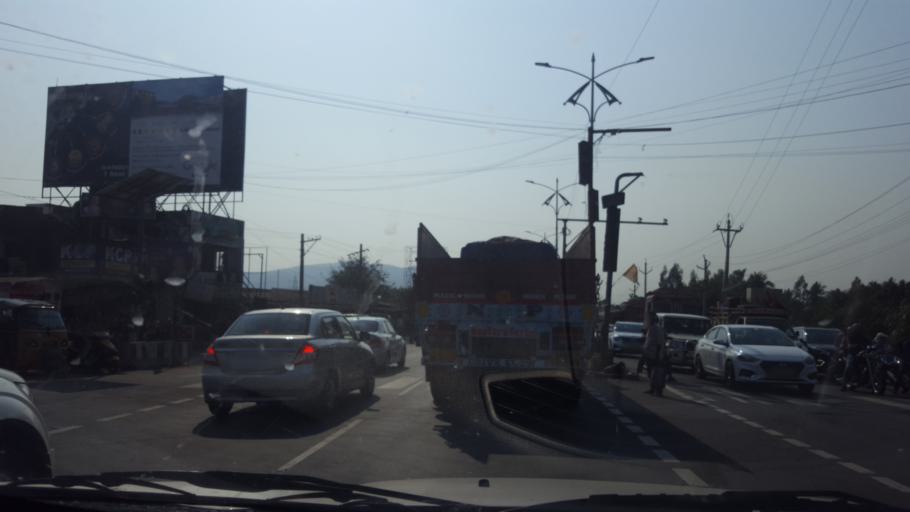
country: IN
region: Andhra Pradesh
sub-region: Vishakhapatnam
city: Anakapalle
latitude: 17.6879
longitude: 83.0968
